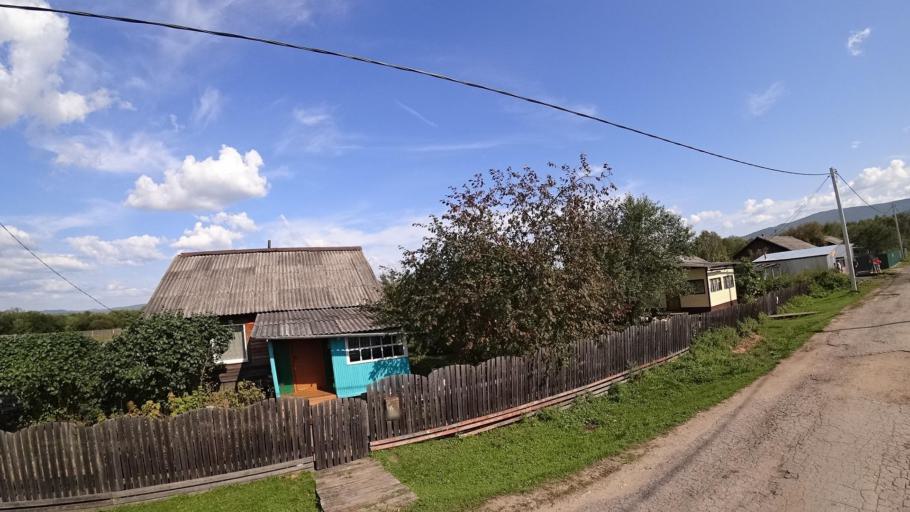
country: RU
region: Jewish Autonomous Oblast
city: Birakan
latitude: 48.9844
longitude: 131.7274
